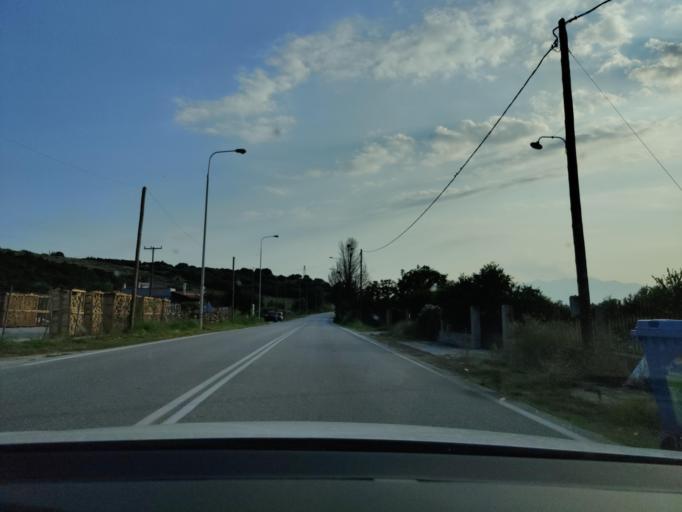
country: GR
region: East Macedonia and Thrace
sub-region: Nomos Kavalas
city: Zygos
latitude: 40.9956
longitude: 24.3822
